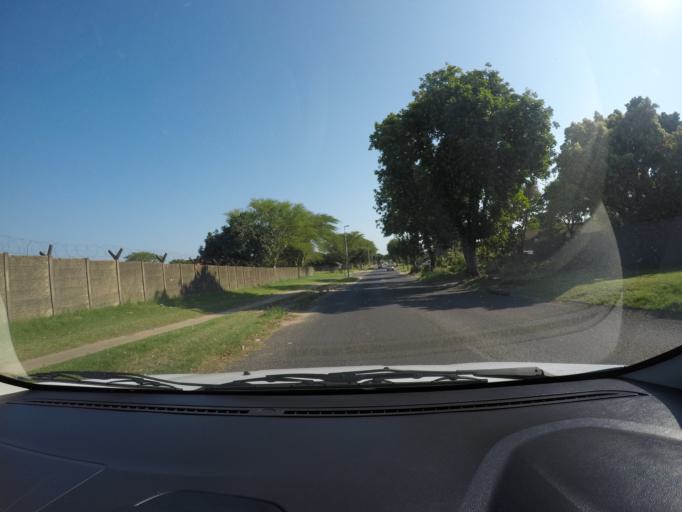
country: ZA
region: KwaZulu-Natal
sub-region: uThungulu District Municipality
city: Richards Bay
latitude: -28.7264
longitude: 32.0419
